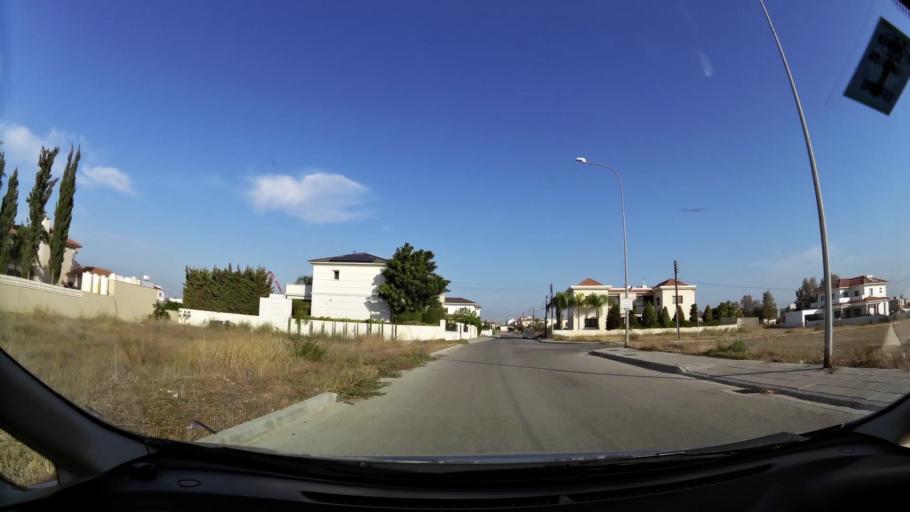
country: CY
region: Larnaka
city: Aradippou
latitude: 34.9348
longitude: 33.5960
